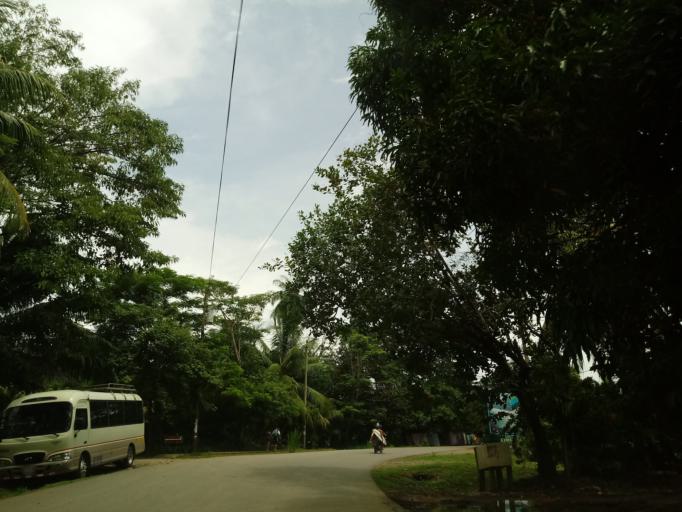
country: CR
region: San Jose
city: Daniel Flores
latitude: 9.1570
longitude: -83.7462
